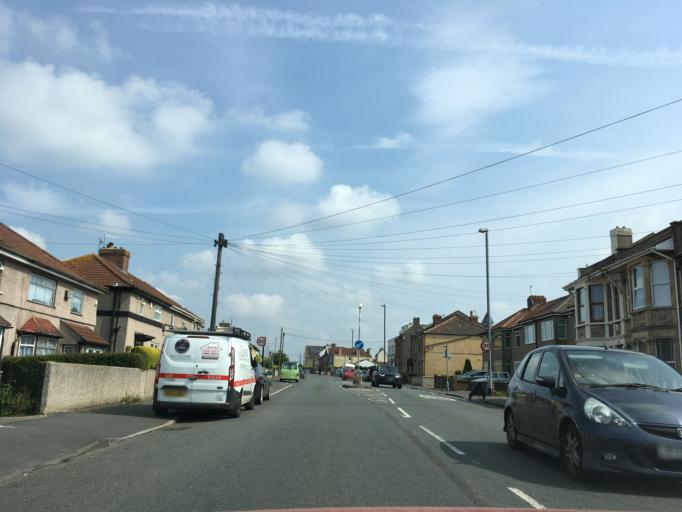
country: GB
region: England
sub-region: Bristol
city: Bristol
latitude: 51.4246
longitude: -2.6146
